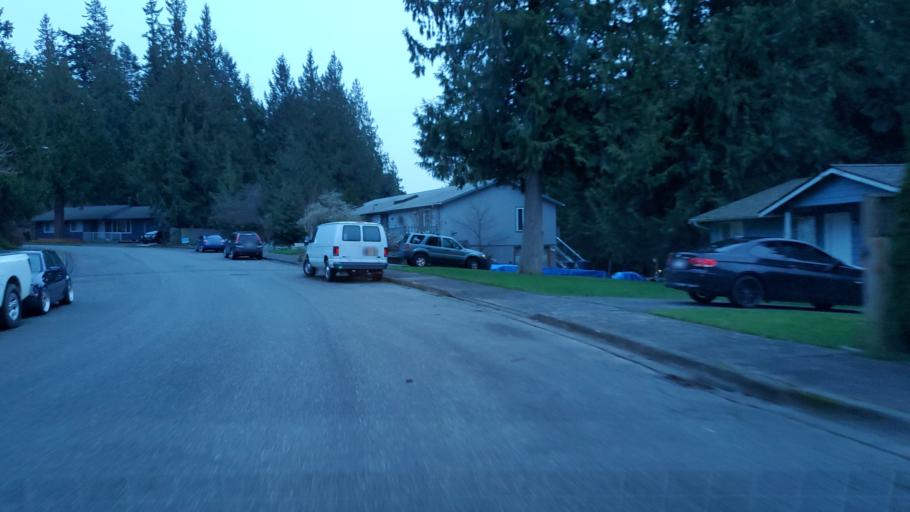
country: US
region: Washington
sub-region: Skagit County
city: Mount Vernon
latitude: 48.4412
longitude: -122.3238
